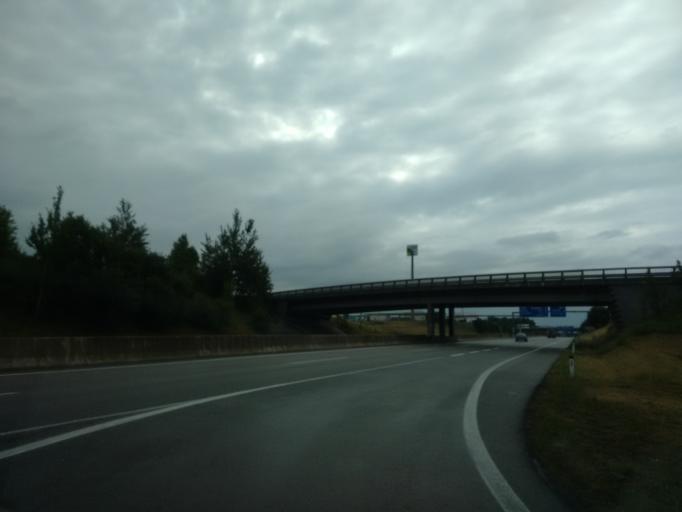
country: AT
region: Upper Austria
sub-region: Wels-Land
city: Sattledt
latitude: 48.0682
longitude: 14.0298
